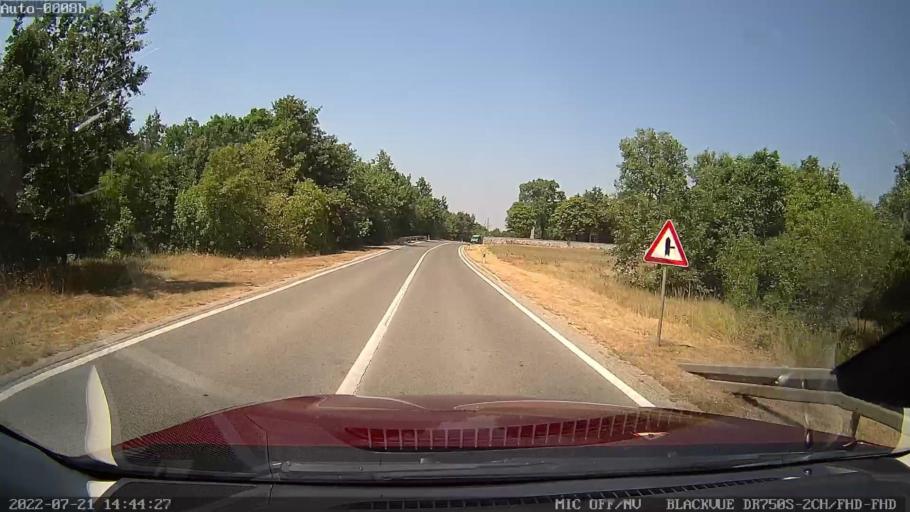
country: HR
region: Istarska
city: Pazin
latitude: 45.1178
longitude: 13.8845
